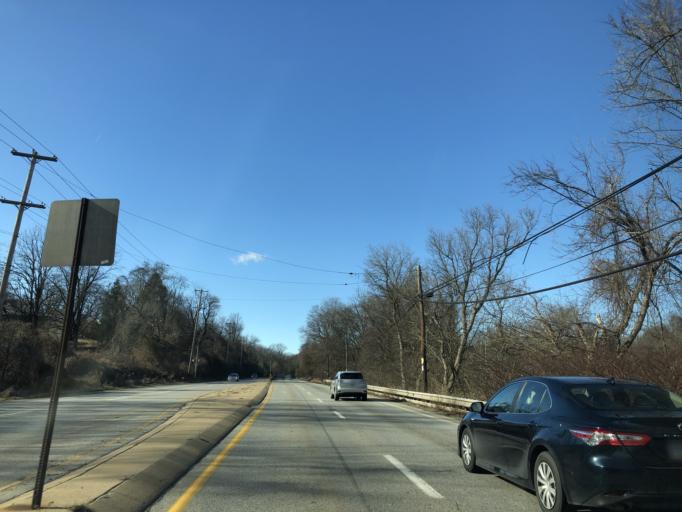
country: US
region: Pennsylvania
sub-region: Chester County
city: West Chester
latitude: 39.8718
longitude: -75.5992
